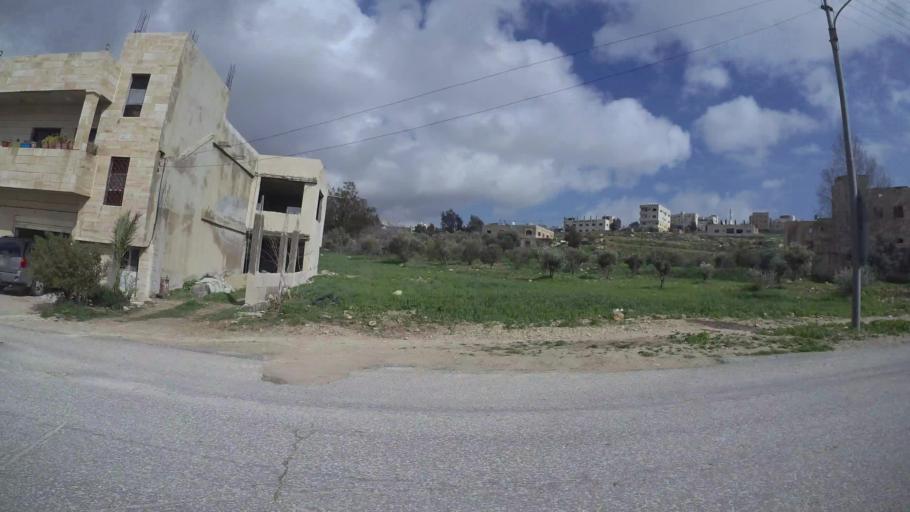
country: JO
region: Amman
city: Al Jubayhah
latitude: 32.0749
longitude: 35.8628
